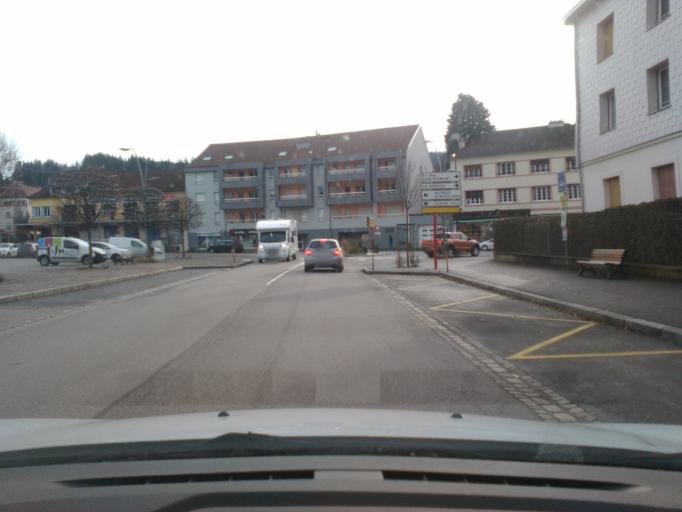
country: FR
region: Lorraine
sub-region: Departement des Vosges
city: Gerardmer
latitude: 48.0719
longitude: 6.8713
